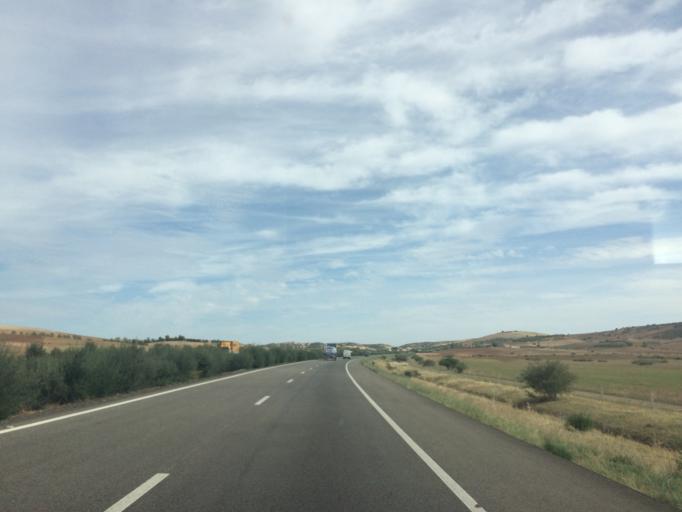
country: MA
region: Rabat-Sale-Zemmour-Zaer
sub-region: Khemisset
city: Khemisset
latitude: 33.8012
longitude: -5.8779
